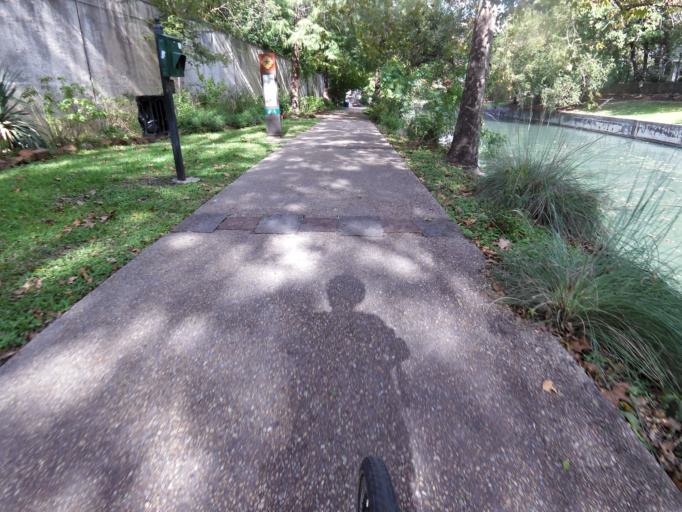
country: US
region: Texas
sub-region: Bexar County
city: San Antonio
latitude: 29.4174
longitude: -98.4936
